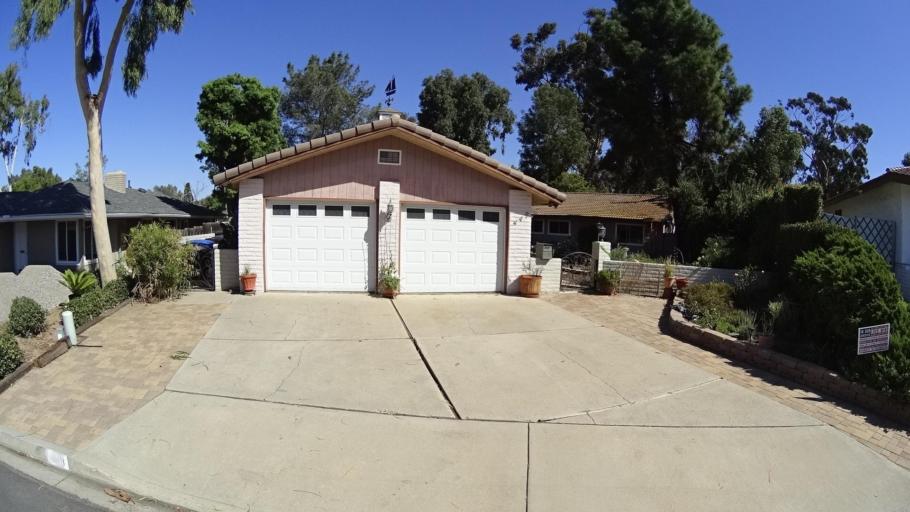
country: US
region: California
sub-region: San Diego County
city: Chula Vista
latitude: 32.6412
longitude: -117.0622
